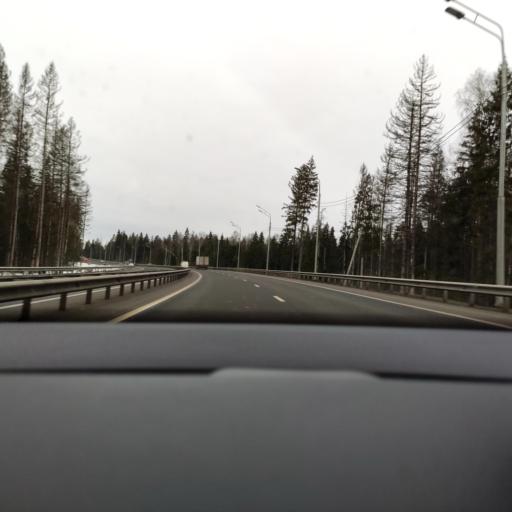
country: RU
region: Moskovskaya
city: Bol'shiye Vyazemy
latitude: 55.6552
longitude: 36.9855
